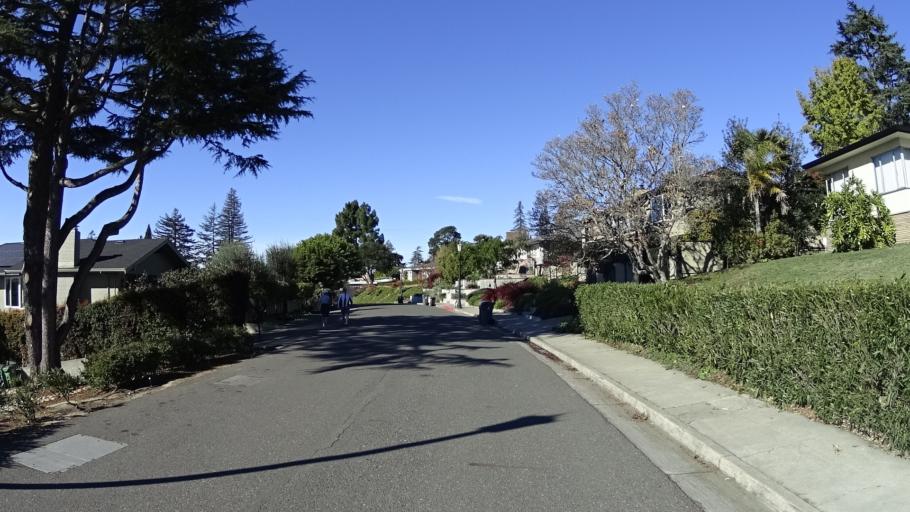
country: US
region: California
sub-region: Alameda County
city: Piedmont
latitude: 37.8224
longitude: -122.2128
